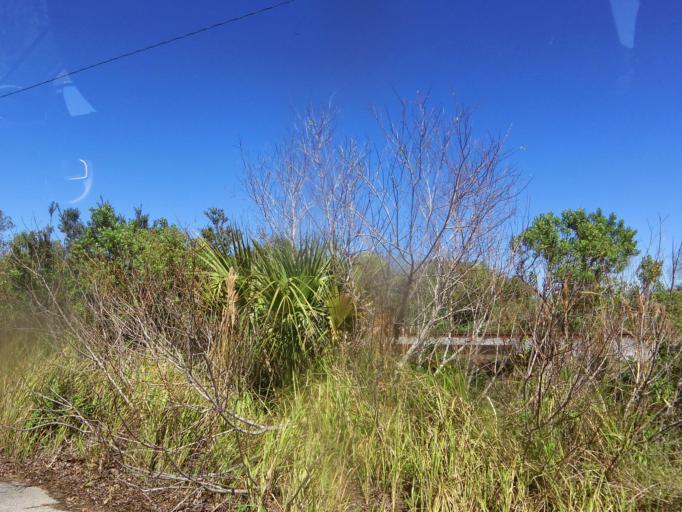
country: US
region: Florida
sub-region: Seminole County
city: Sanford
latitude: 28.8180
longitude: -81.3062
